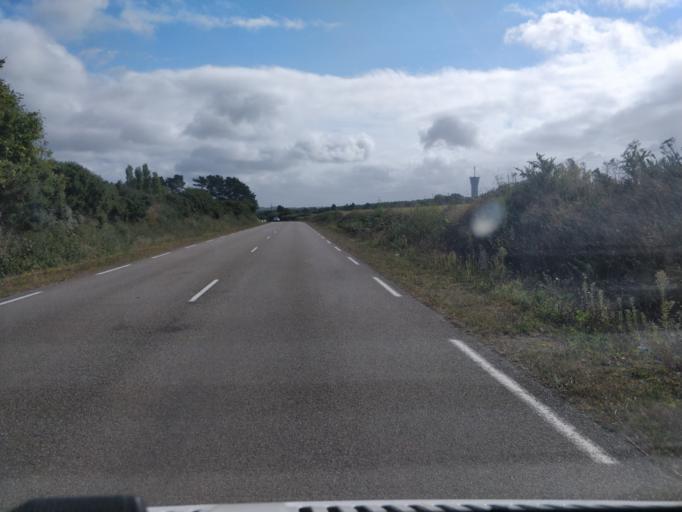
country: FR
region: Brittany
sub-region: Departement du Finistere
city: Plozevet
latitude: 47.9949
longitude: -4.3874
